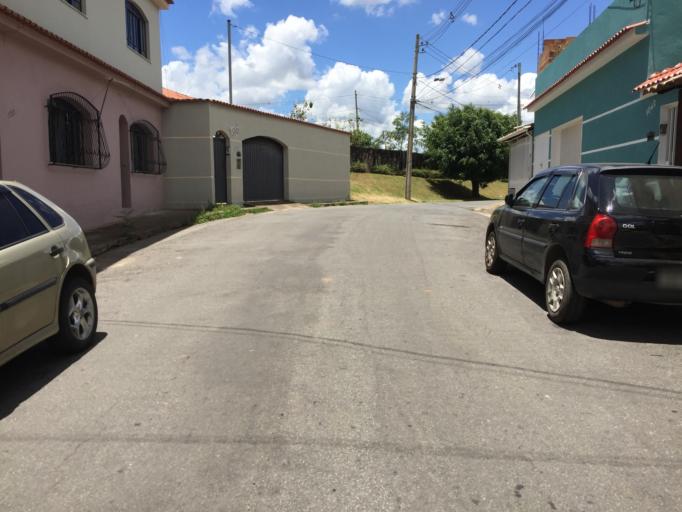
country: BR
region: Minas Gerais
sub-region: Sao Joao Del Rei
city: Sao Joao del Rei
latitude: -21.1450
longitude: -44.2673
